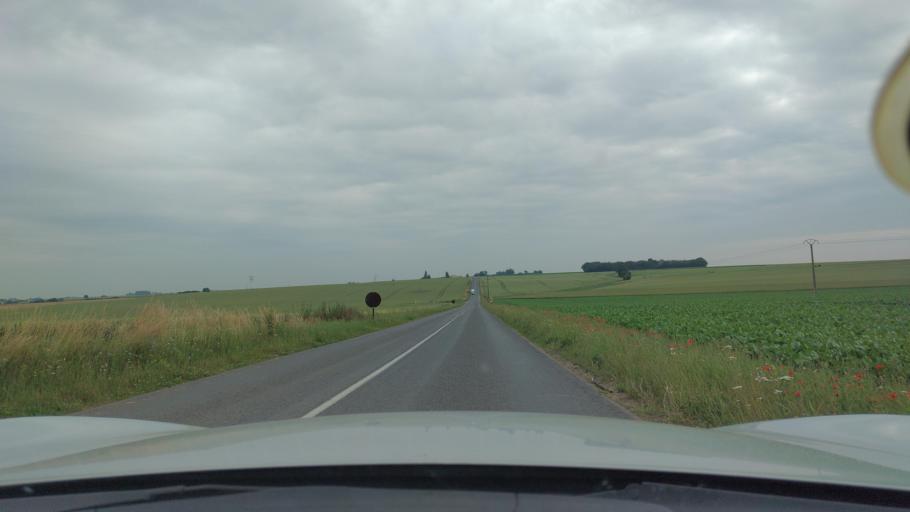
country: FR
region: Ile-de-France
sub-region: Departement de Seine-et-Marne
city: Cregy-les-Meaux
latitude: 49.0189
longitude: 2.8851
